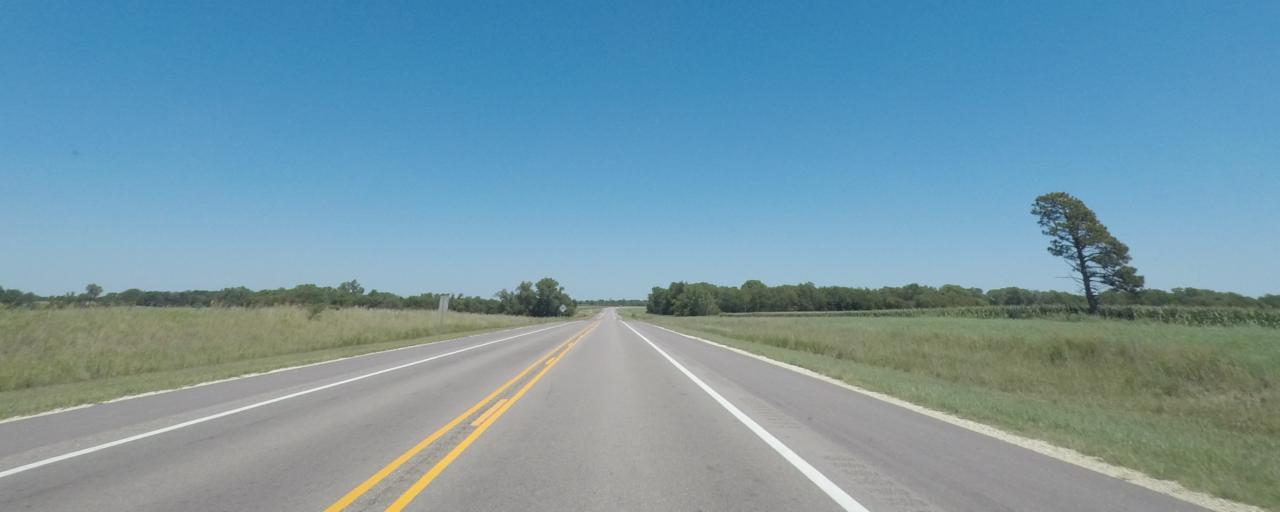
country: US
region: Kansas
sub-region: Marion County
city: Peabody
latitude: 38.1674
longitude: -97.1987
